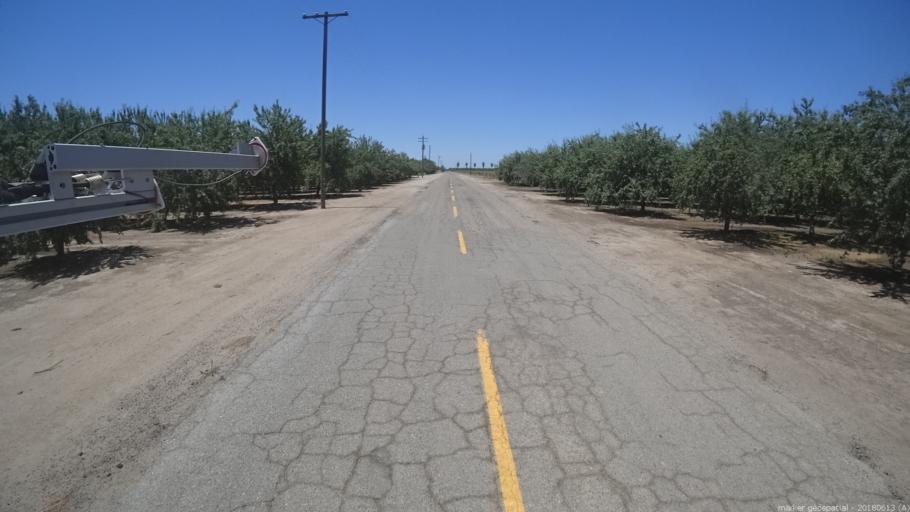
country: US
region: California
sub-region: Madera County
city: Chowchilla
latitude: 37.0618
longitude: -120.2855
